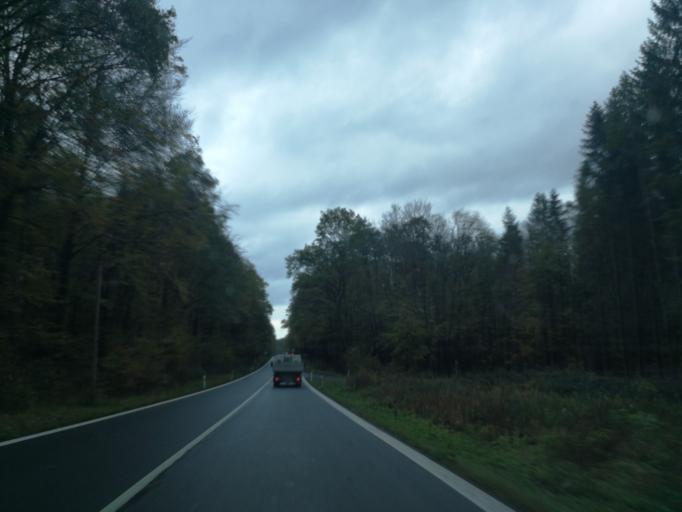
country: CZ
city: Hodslavice
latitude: 49.5198
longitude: 18.0136
